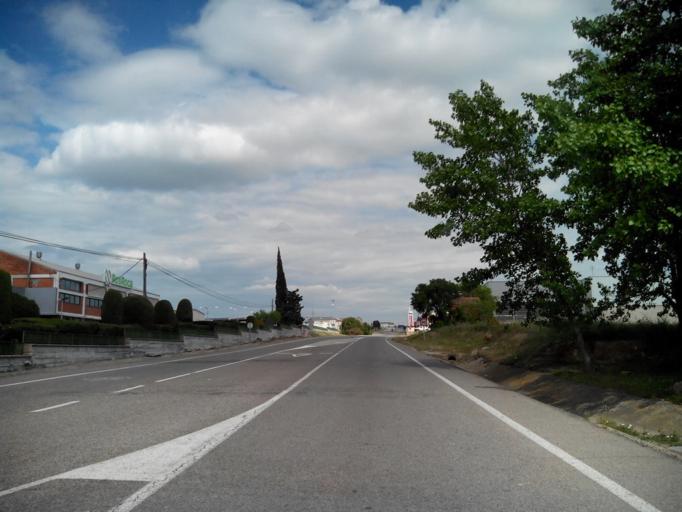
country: ES
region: Catalonia
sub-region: Provincia de Lleida
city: Tarrega
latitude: 41.6531
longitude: 1.1504
